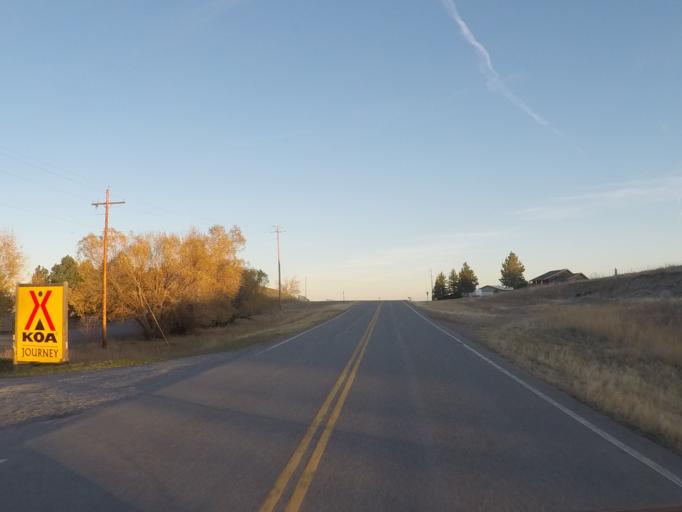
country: US
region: Montana
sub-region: Sweet Grass County
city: Big Timber
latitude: 45.7731
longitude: -109.8001
